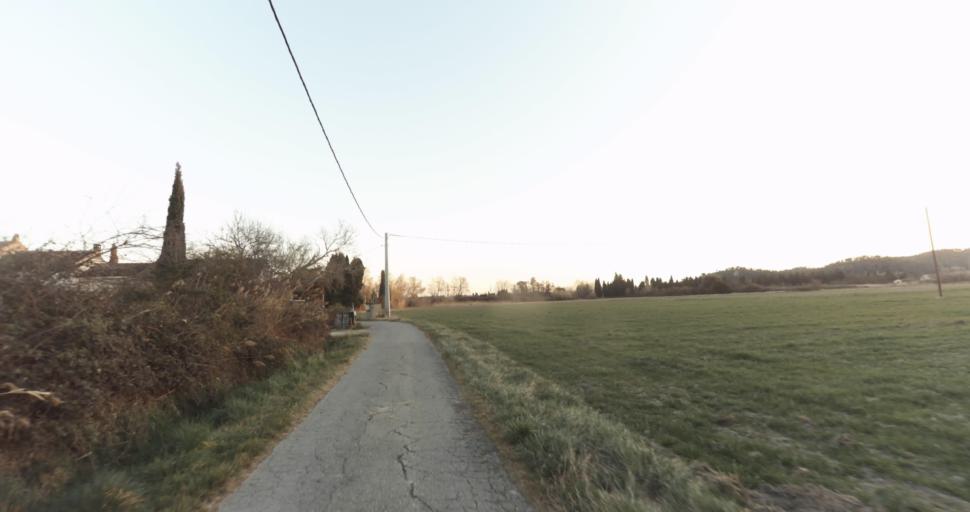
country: FR
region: Provence-Alpes-Cote d'Azur
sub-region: Departement des Bouches-du-Rhone
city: Rognonas
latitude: 43.8898
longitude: 4.7766
